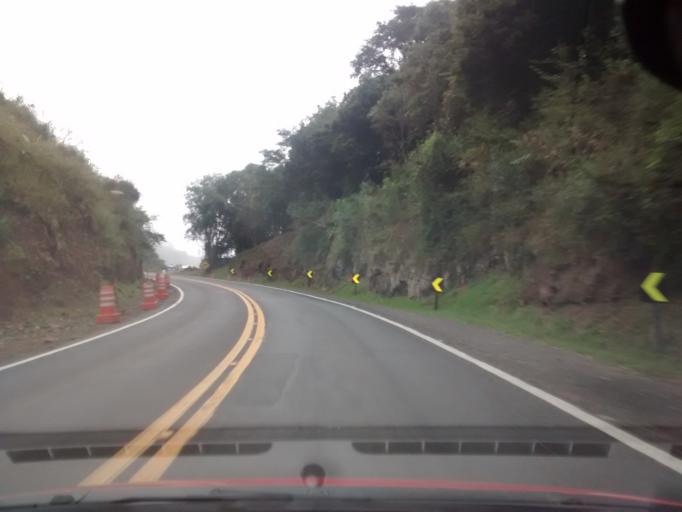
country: BR
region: Rio Grande do Sul
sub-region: Vacaria
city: Estrela
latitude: -28.1982
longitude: -50.7220
